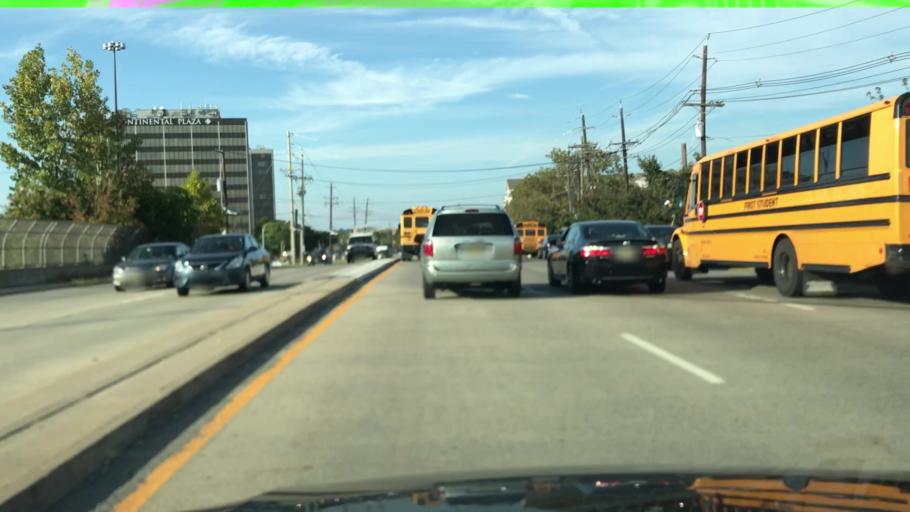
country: US
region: New Jersey
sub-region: Bergen County
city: Teaneck
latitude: 40.9061
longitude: -74.0333
